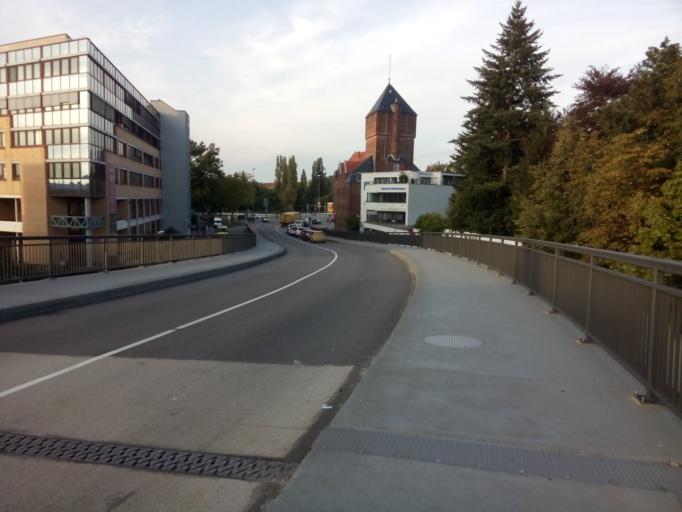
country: DE
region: Baden-Wuerttemberg
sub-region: Karlsruhe Region
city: Karlsruhe
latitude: 49.0028
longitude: 8.3651
